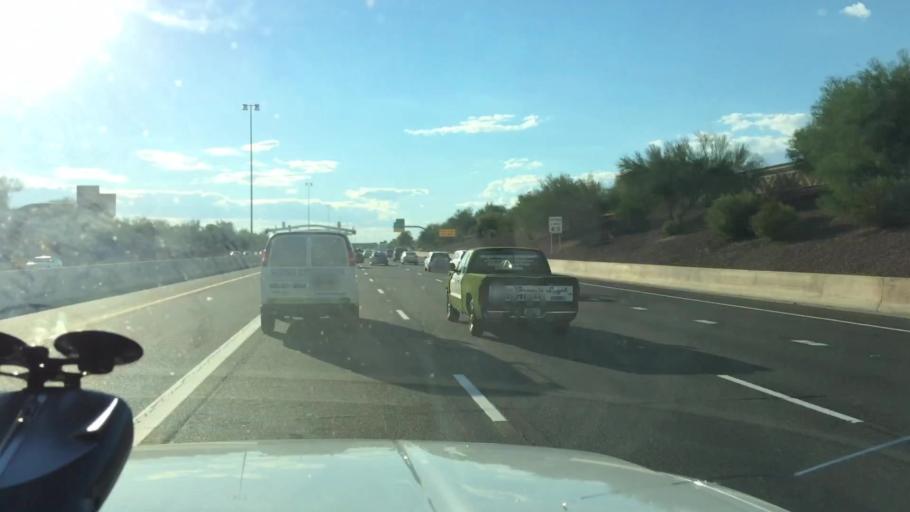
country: US
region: Arizona
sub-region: Maricopa County
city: Peoria
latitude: 33.6686
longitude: -112.2114
